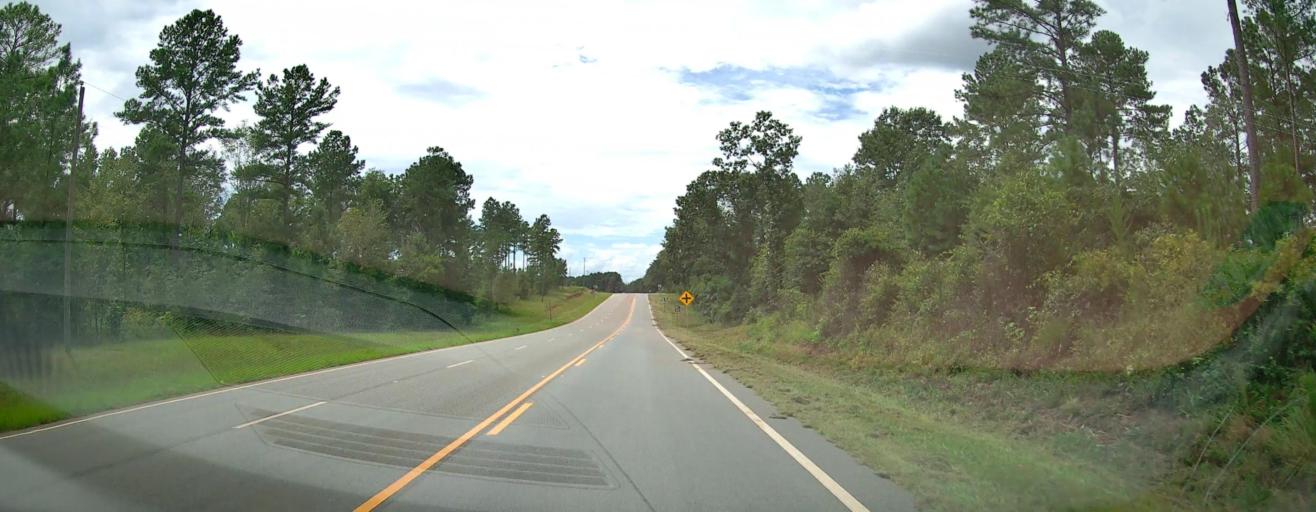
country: US
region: Georgia
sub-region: Macon County
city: Oglethorpe
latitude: 32.2829
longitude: -84.1540
